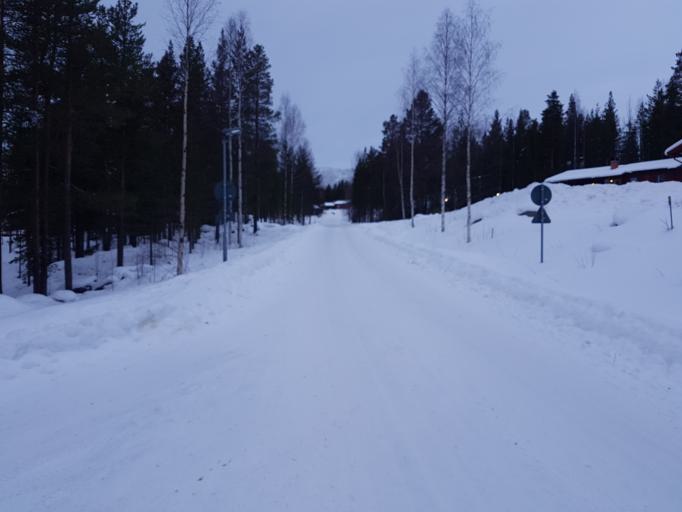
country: SE
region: Jaemtland
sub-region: Harjedalens Kommun
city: Sveg
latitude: 62.4203
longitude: 13.9486
